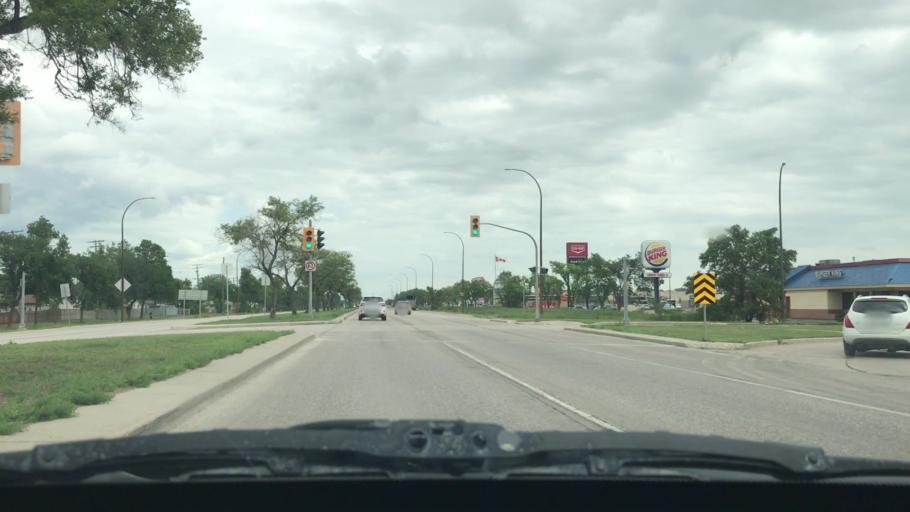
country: CA
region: Manitoba
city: Winnipeg
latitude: 49.8560
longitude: -97.0751
